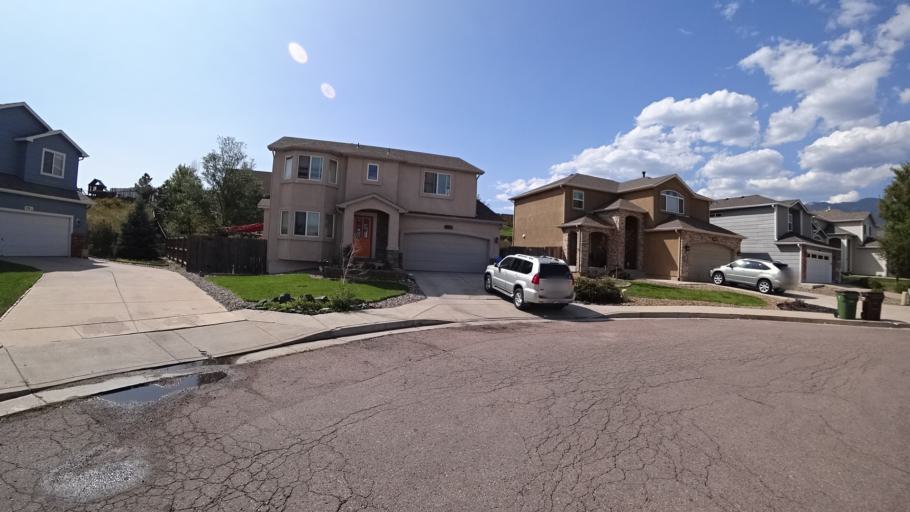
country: US
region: Colorado
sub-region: El Paso County
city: Colorado Springs
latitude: 38.8270
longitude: -104.8470
